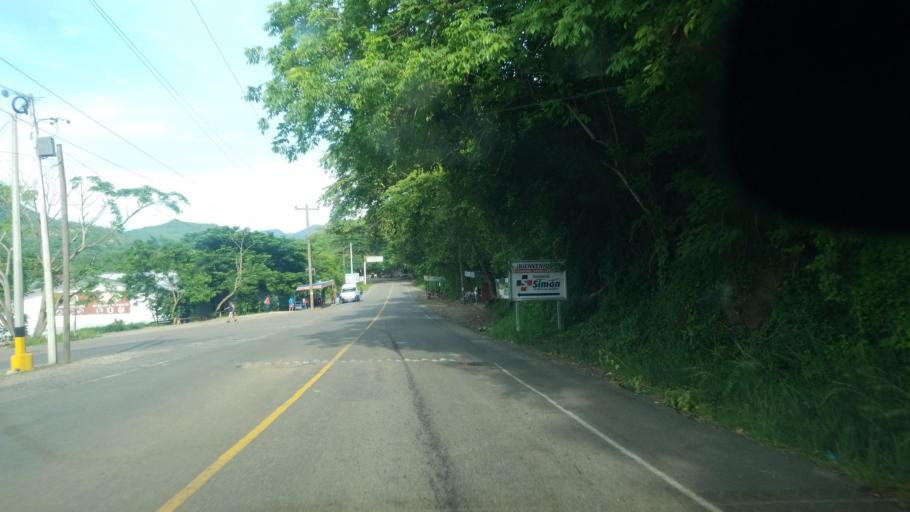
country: HN
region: Santa Barbara
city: Trinidad
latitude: 15.1392
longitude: -88.2343
